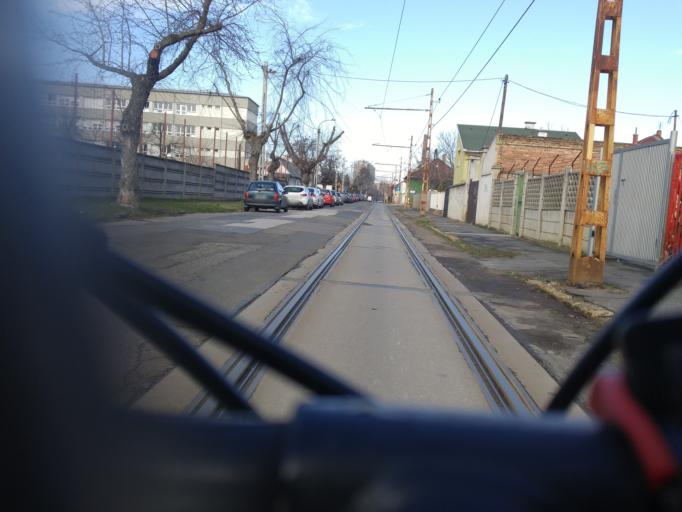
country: HU
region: Budapest
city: Budapest XX. keruelet
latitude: 47.4321
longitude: 19.1130
